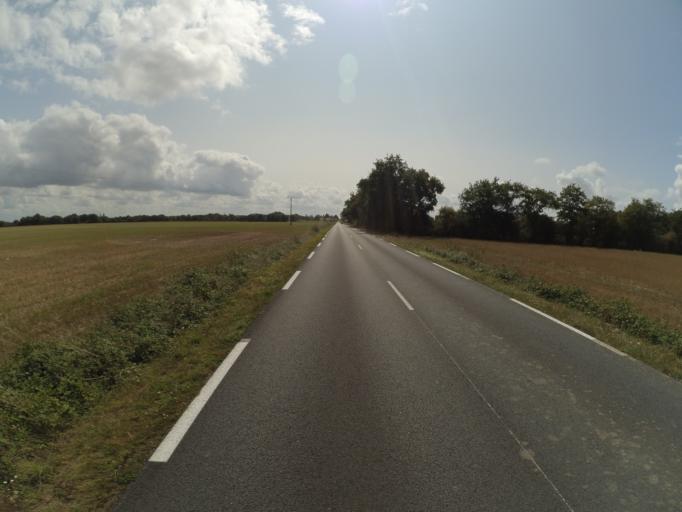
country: FR
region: Pays de la Loire
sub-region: Departement de la Vendee
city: Montaigu
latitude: 47.0095
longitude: -1.2812
